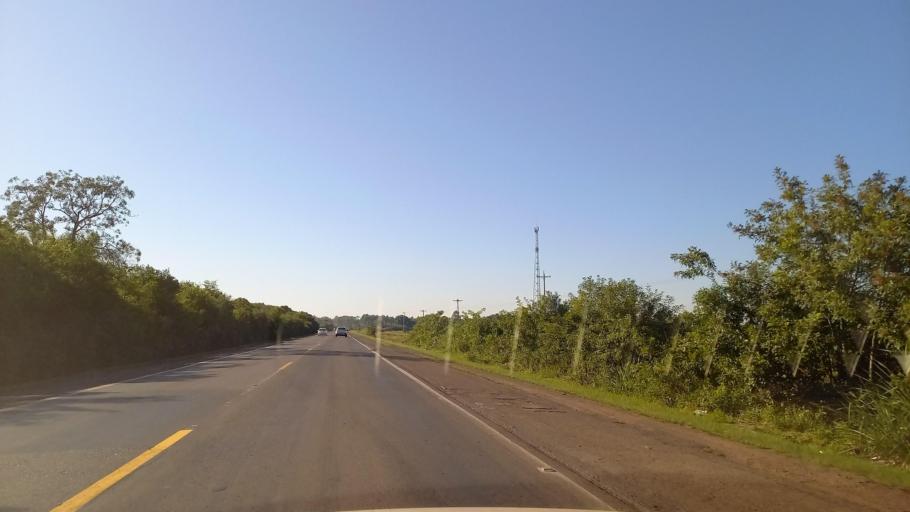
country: BR
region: Rio Grande do Sul
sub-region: Venancio Aires
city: Venancio Aires
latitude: -29.6664
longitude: -52.0492
